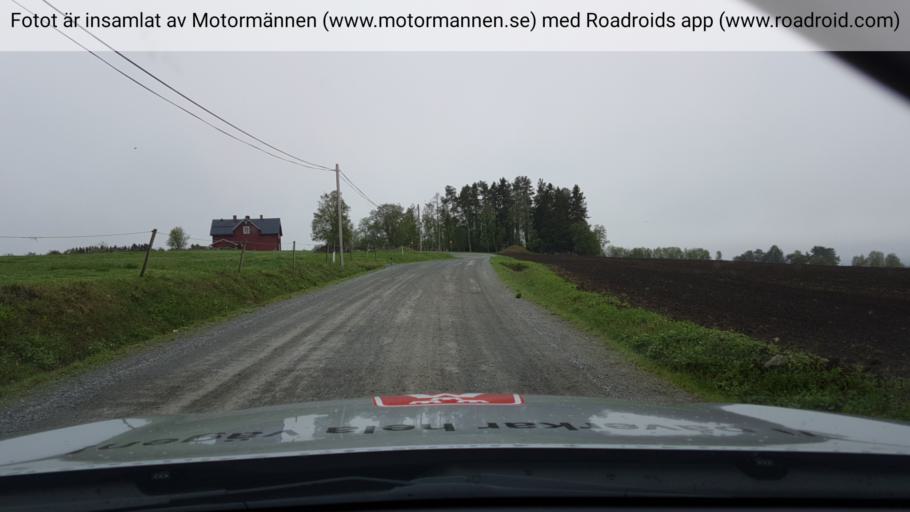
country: SE
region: Jaemtland
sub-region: Bergs Kommun
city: Hoverberg
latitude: 63.0047
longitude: 14.3901
